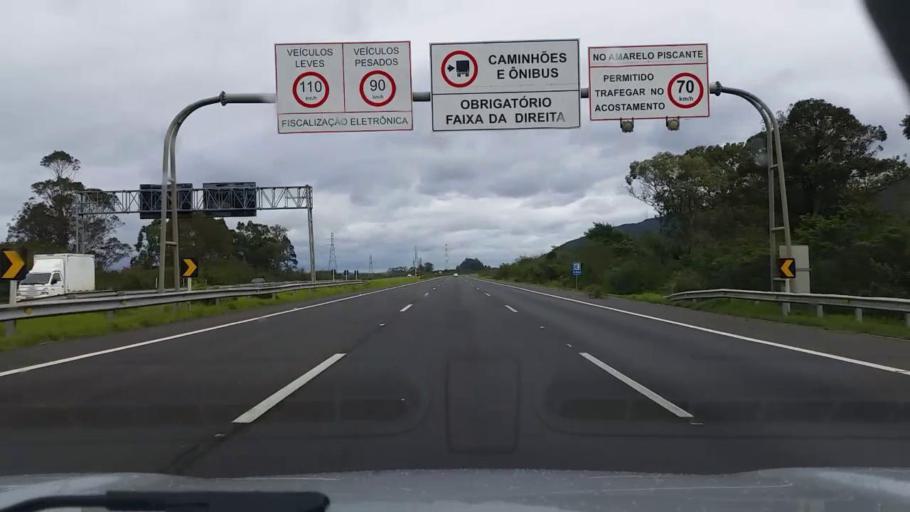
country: BR
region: Rio Grande do Sul
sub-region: Osorio
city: Osorio
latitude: -29.8980
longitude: -50.3053
